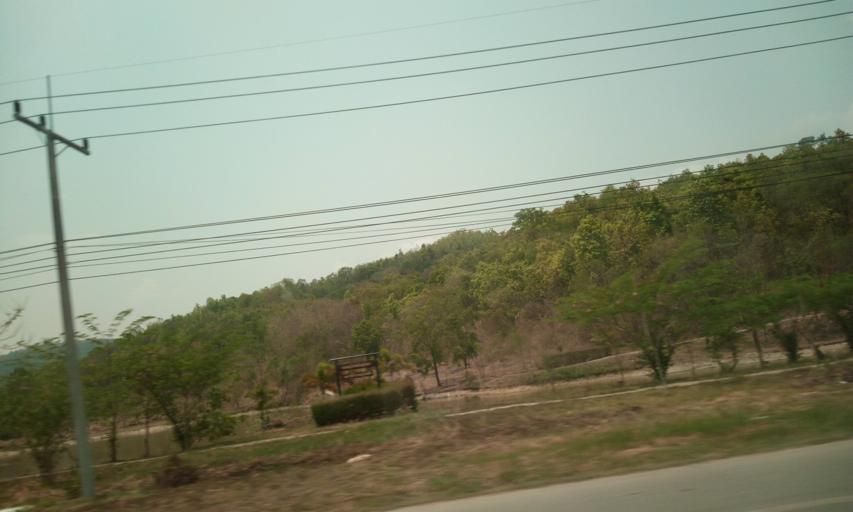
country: TH
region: Chiang Rai
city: Thoeng
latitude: 19.6919
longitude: 100.1721
